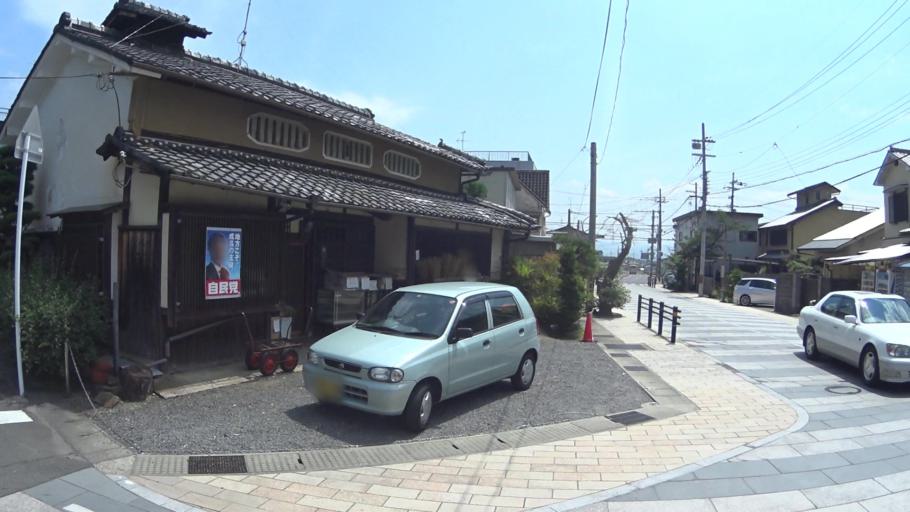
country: JP
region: Kyoto
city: Muko
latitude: 34.9389
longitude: 135.6787
